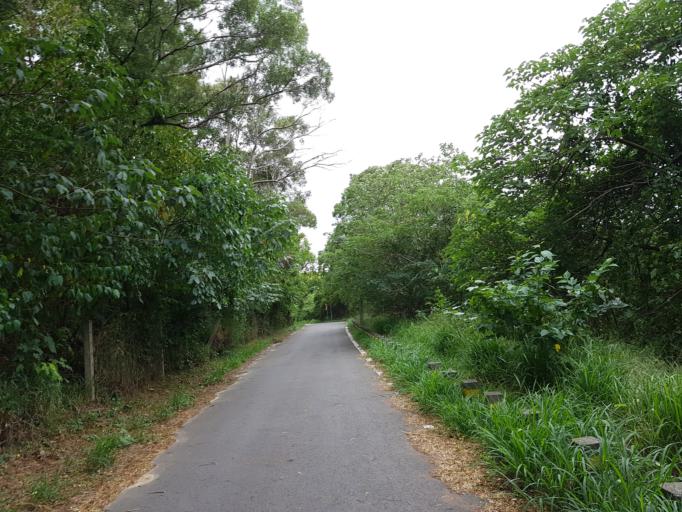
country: TW
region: Taiwan
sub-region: Hsinchu
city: Hsinchu
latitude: 24.7543
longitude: 120.9507
